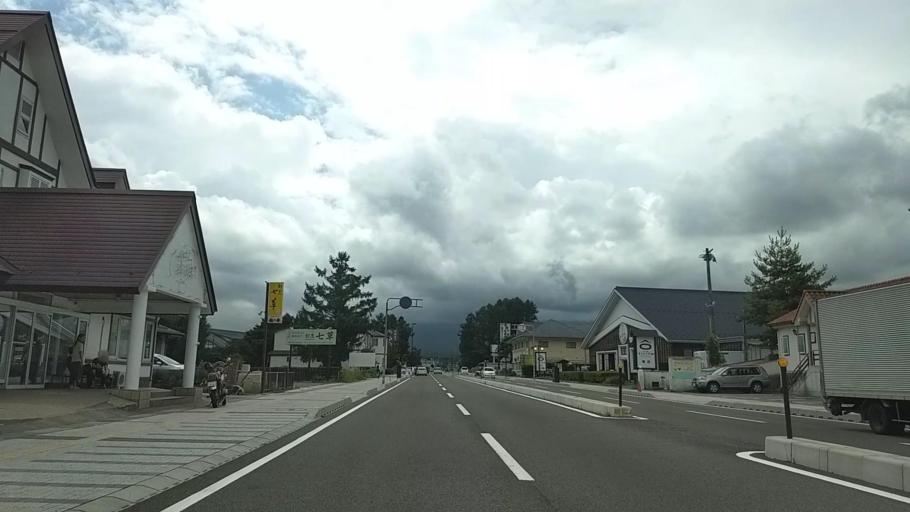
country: JP
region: Yamanashi
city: Fujikawaguchiko
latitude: 35.4973
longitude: 138.7561
